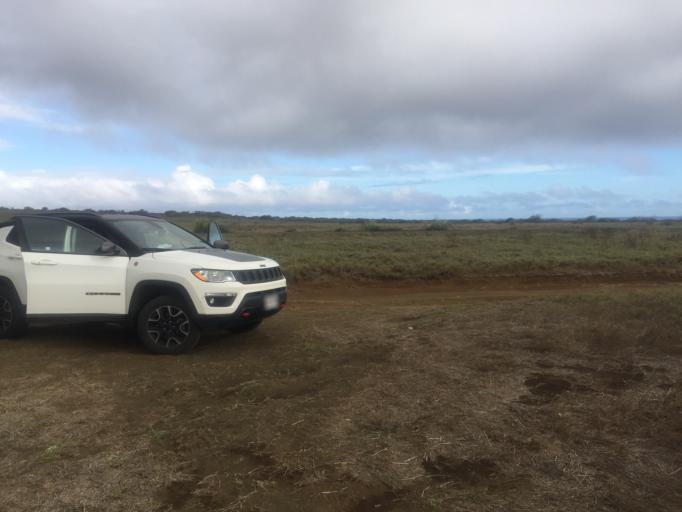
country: US
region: Hawaii
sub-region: Hawaii County
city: Hawaiian Ocean View
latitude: 18.9214
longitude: -155.6835
